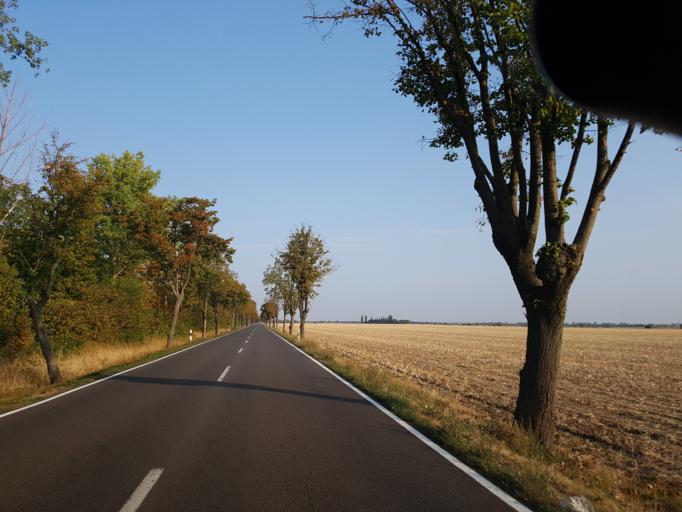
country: DE
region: Saxony-Anhalt
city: Bad Schmiedeberg
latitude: 51.7631
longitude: 12.7413
